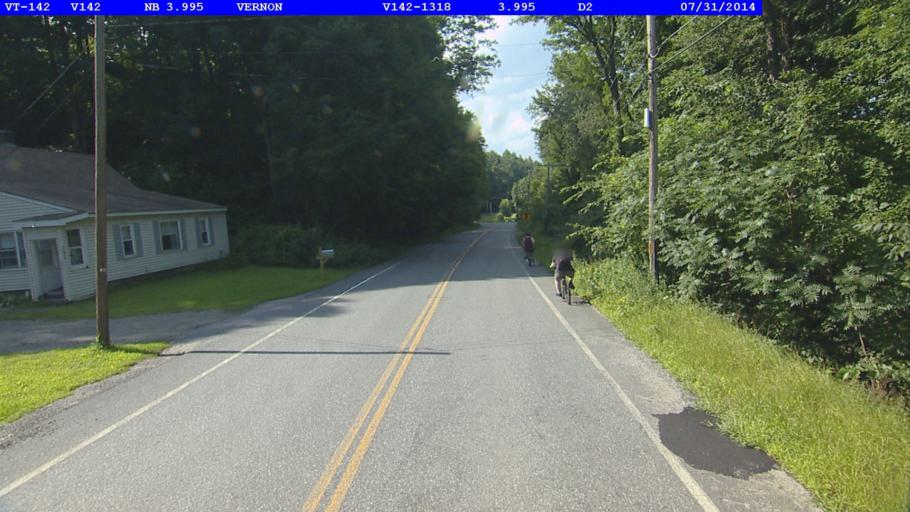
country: US
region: New Hampshire
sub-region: Cheshire County
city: Hinsdale
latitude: 42.7632
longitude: -72.5149
